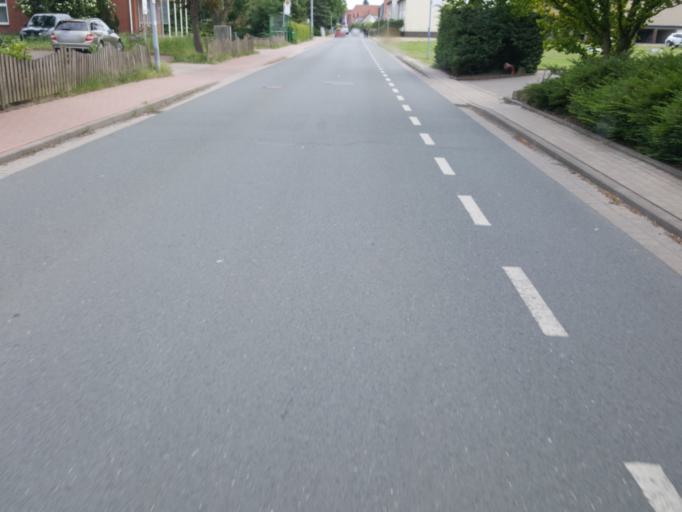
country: DE
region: Lower Saxony
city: Stolzenau
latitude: 52.5162
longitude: 9.0671
